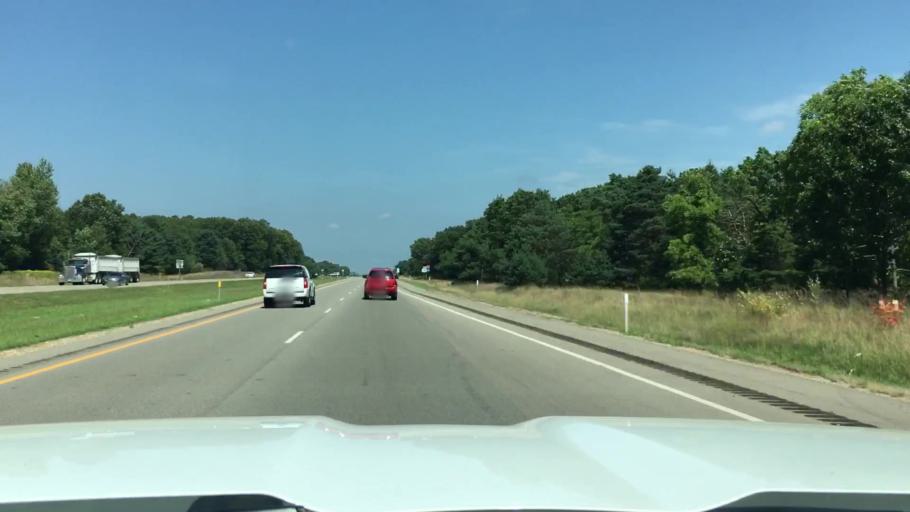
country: US
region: Michigan
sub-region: Kalamazoo County
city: Portage
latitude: 42.2048
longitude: -85.6443
